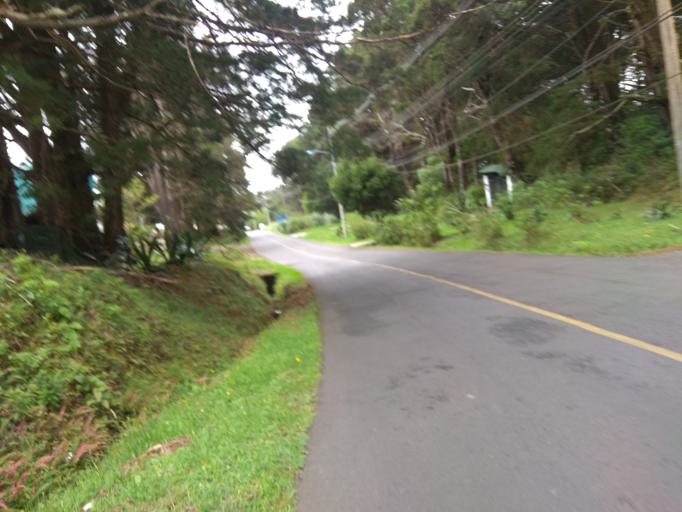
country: CR
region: Heredia
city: San Josecito
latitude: 10.0683
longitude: -84.0844
